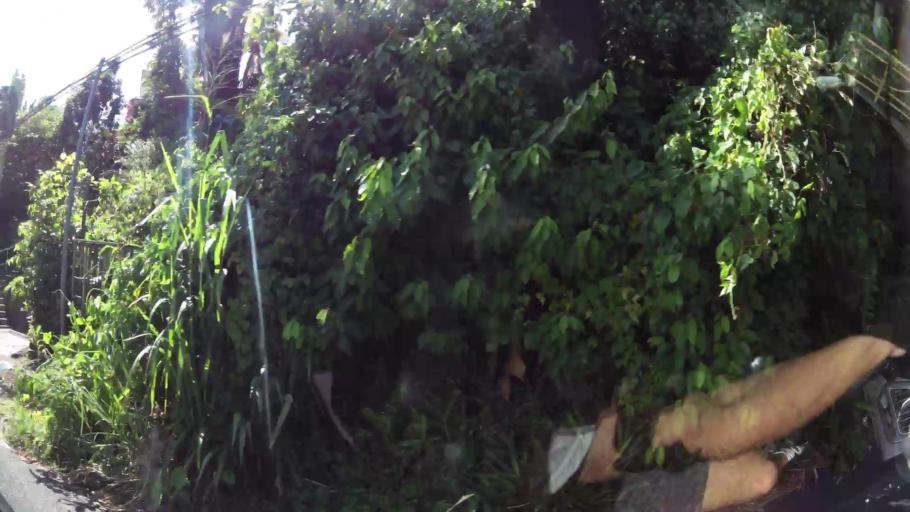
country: CR
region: Puntarenas
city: Quepos
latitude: 9.4022
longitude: -84.1603
